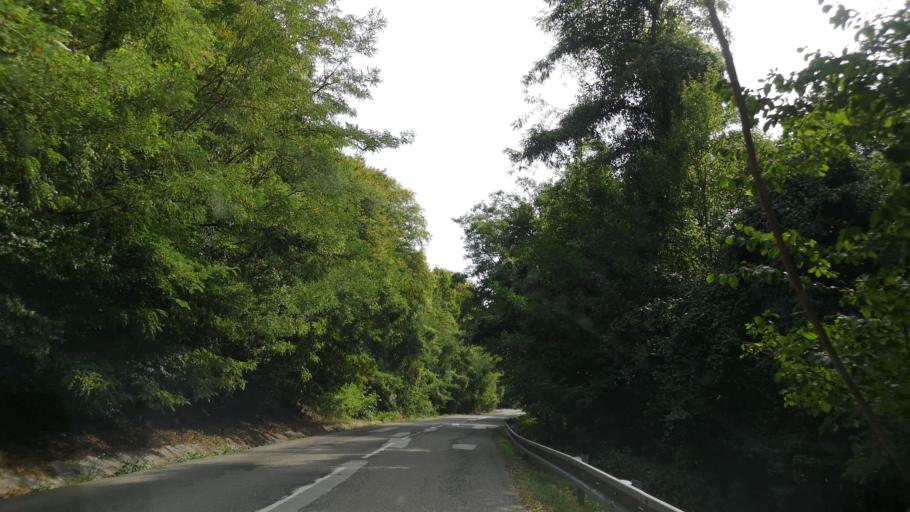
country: SK
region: Banskobystricky
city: Revuca
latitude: 48.5857
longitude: 20.0774
